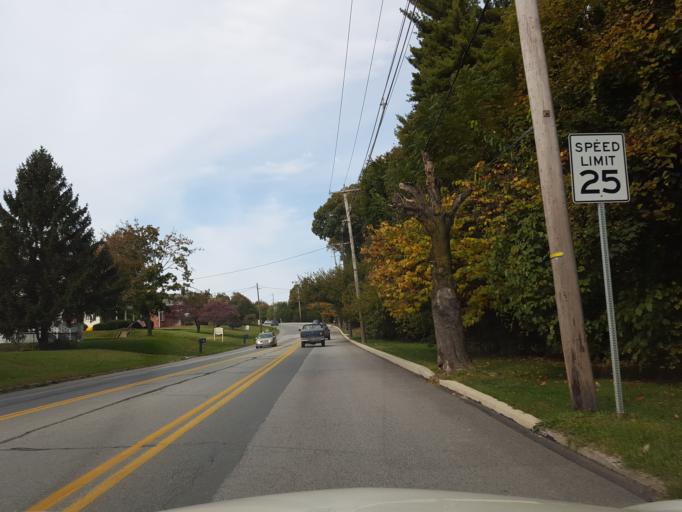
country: US
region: Pennsylvania
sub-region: York County
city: Dallastown
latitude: 39.8973
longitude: -76.6246
